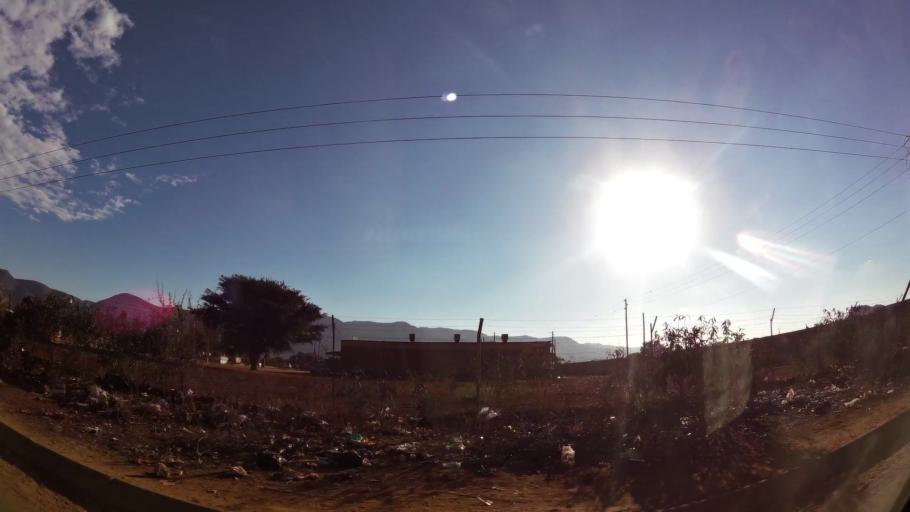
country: ZA
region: Limpopo
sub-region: Waterberg District Municipality
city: Mokopane
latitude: -24.1801
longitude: 28.9832
